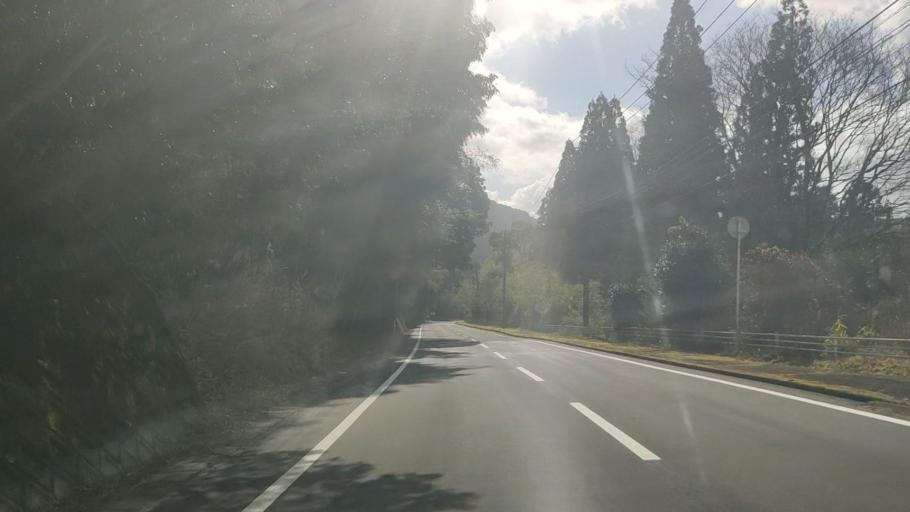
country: JP
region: Kagoshima
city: Okuchi-shinohara
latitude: 31.9848
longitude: 130.7429
